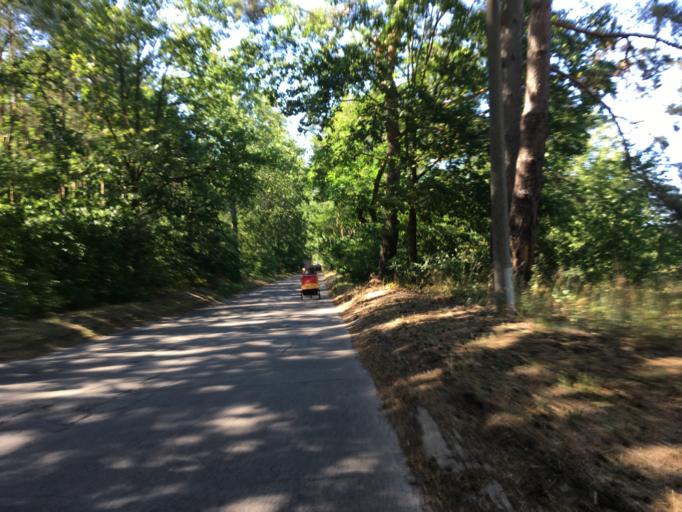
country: DE
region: Brandenburg
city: Schulzendorf
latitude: 52.3535
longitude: 13.5923
